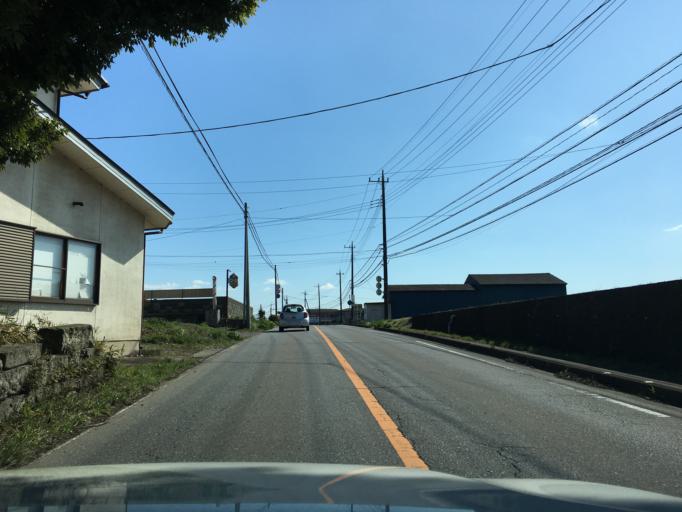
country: JP
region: Tochigi
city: Karasuyama
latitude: 36.7403
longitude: 140.1358
